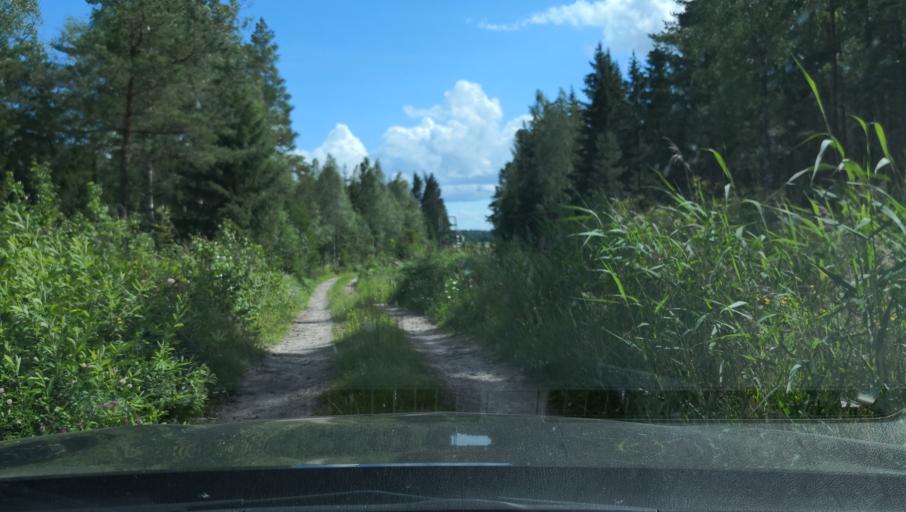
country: SE
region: Vaestmanland
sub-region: Kungsors Kommun
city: Kungsoer
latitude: 59.3333
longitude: 16.0643
